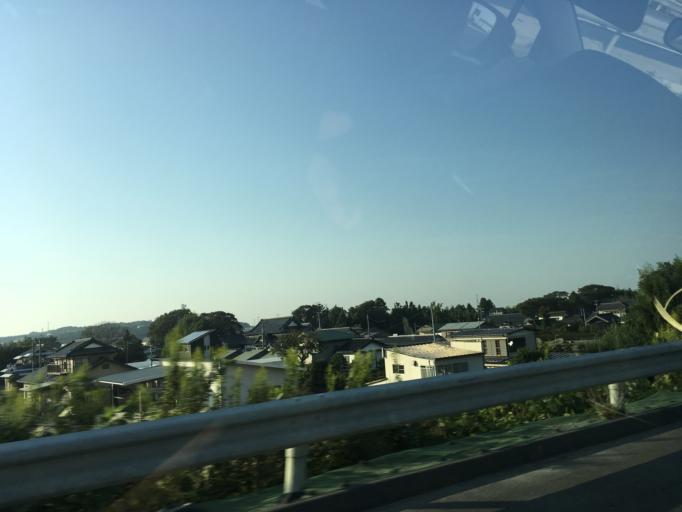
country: JP
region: Miyagi
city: Ishinomaki
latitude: 38.4517
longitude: 141.2713
